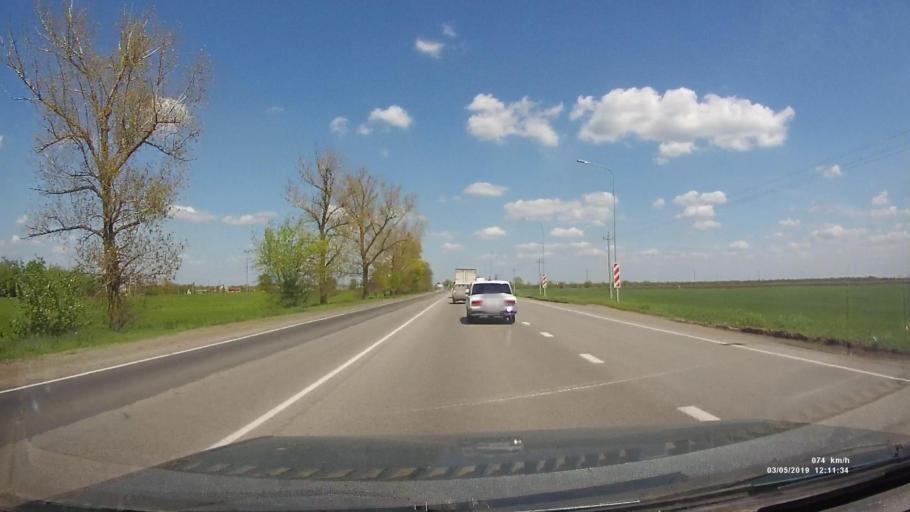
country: RU
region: Rostov
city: Bagayevskaya
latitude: 47.3122
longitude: 40.5396
